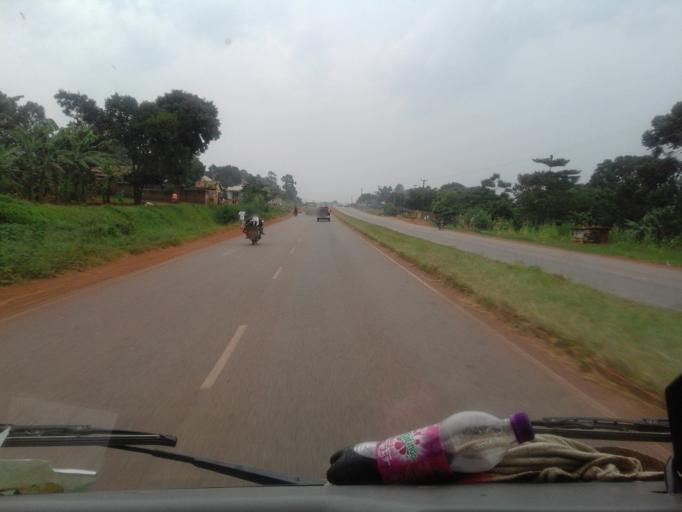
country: UG
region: Eastern Region
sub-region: Jinja District
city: Bugembe
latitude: 0.4720
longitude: 33.2537
